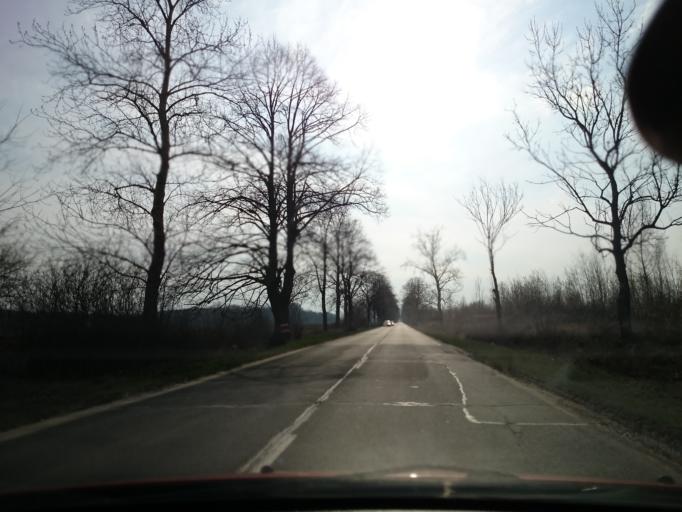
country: PL
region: Opole Voivodeship
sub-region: Powiat nyski
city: Paczkow
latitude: 50.4850
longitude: 16.9849
